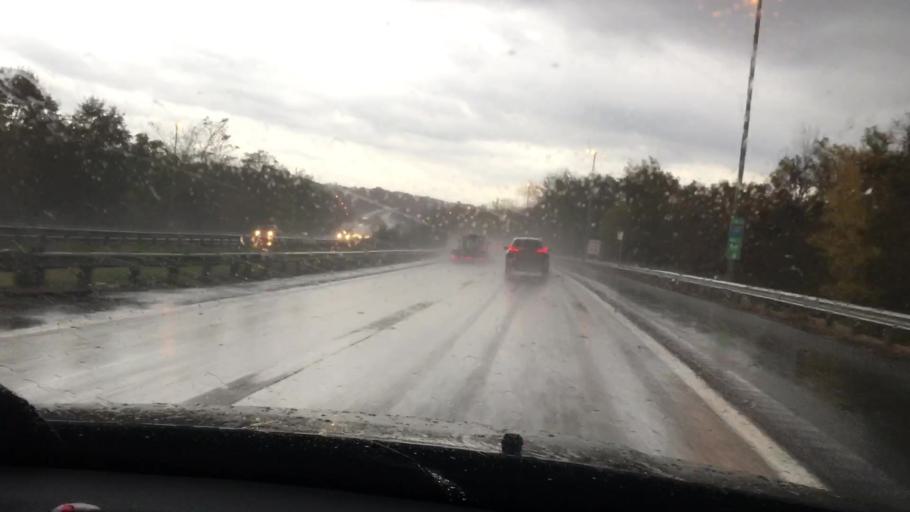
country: US
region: New York
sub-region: Rockland County
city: Suffern
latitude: 41.1012
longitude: -74.1695
